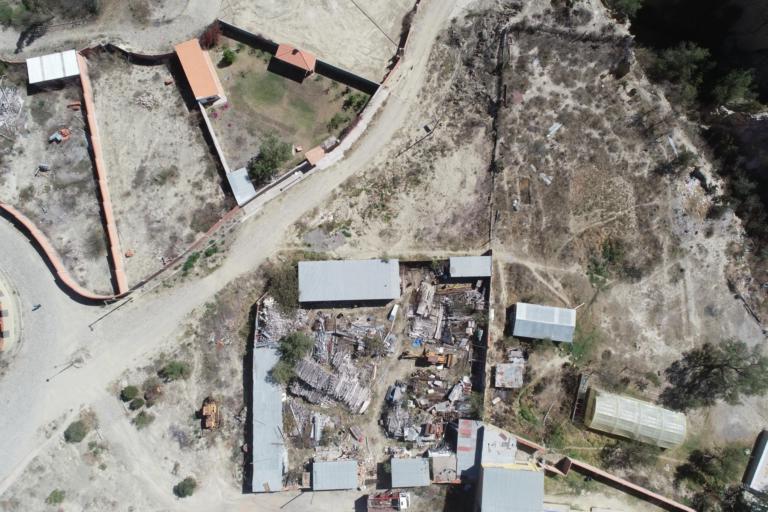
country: BO
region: La Paz
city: La Paz
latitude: -16.6349
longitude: -68.0489
